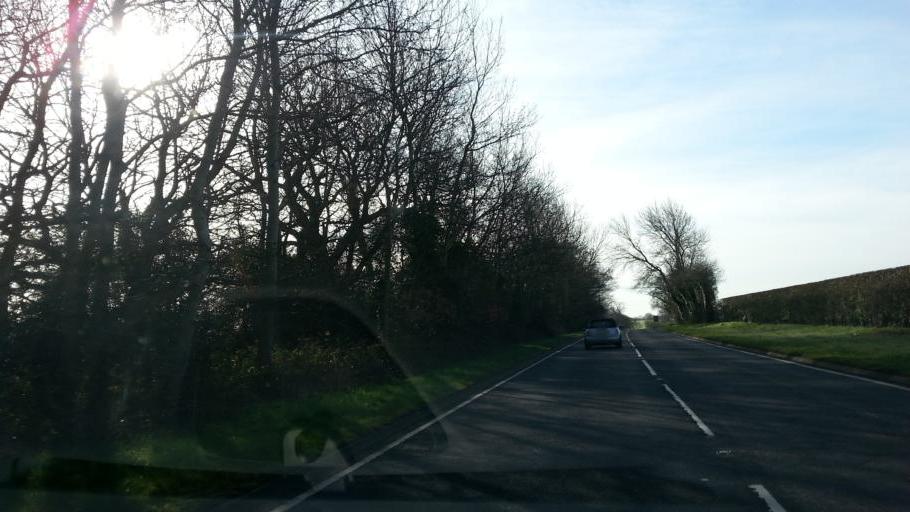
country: GB
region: England
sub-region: Leicestershire
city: Hinckley
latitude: 52.5110
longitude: -1.3664
